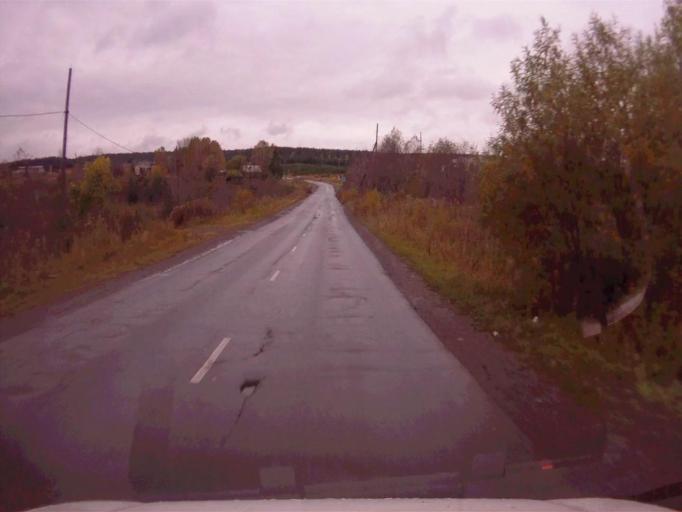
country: RU
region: Chelyabinsk
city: Verkhniy Ufaley
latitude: 56.0600
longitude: 60.1872
